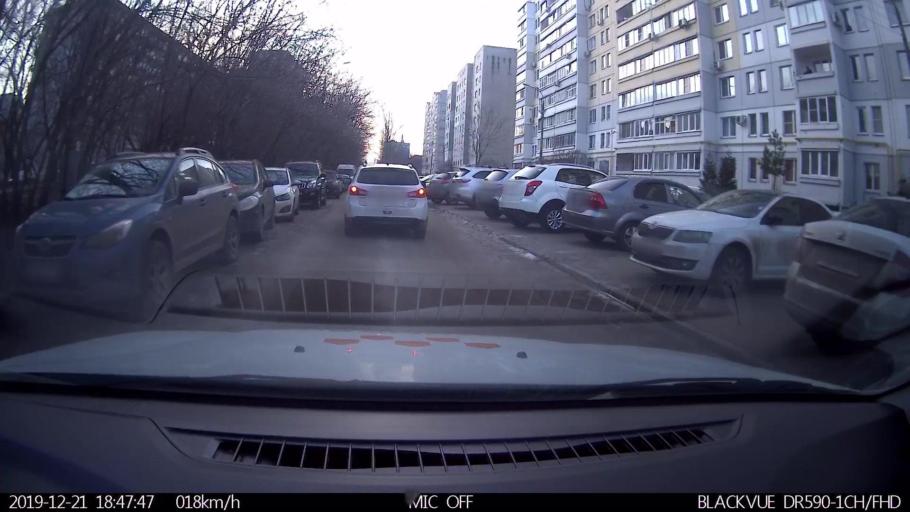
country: RU
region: Nizjnij Novgorod
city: Nizhniy Novgorod
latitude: 56.3275
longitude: 43.9286
